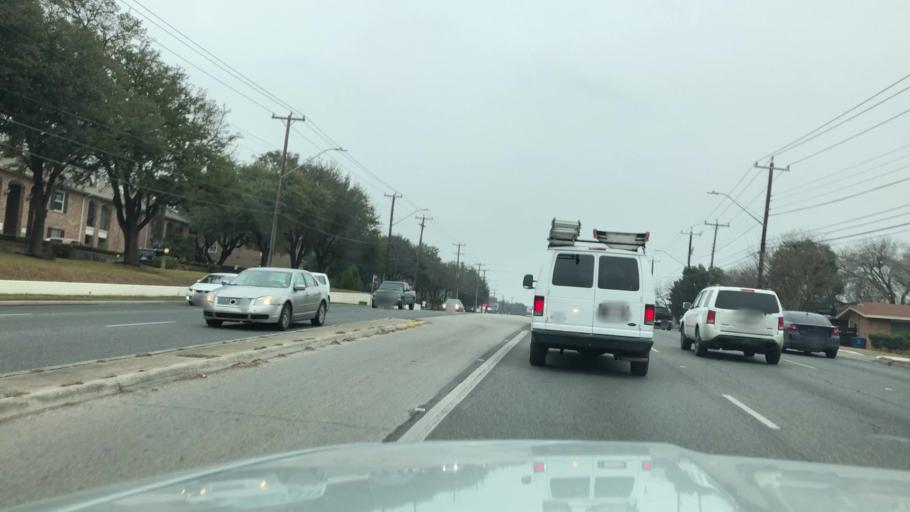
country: US
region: Texas
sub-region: Bexar County
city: Balcones Heights
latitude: 29.4962
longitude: -98.5734
